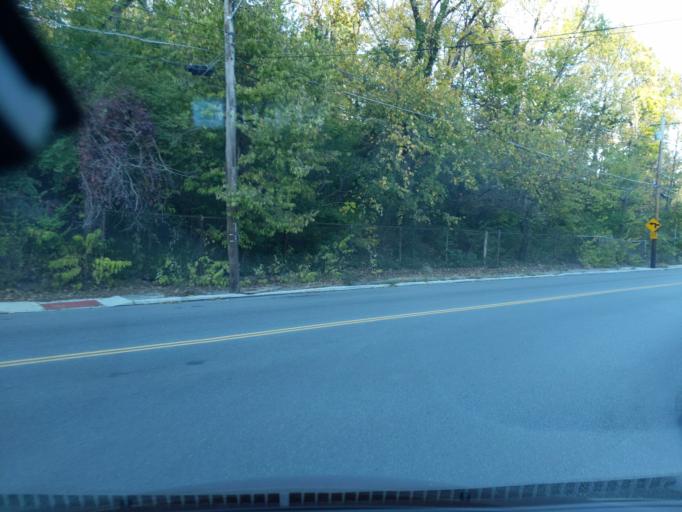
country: US
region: Kentucky
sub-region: Campbell County
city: Dayton
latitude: 39.1264
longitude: -84.4722
